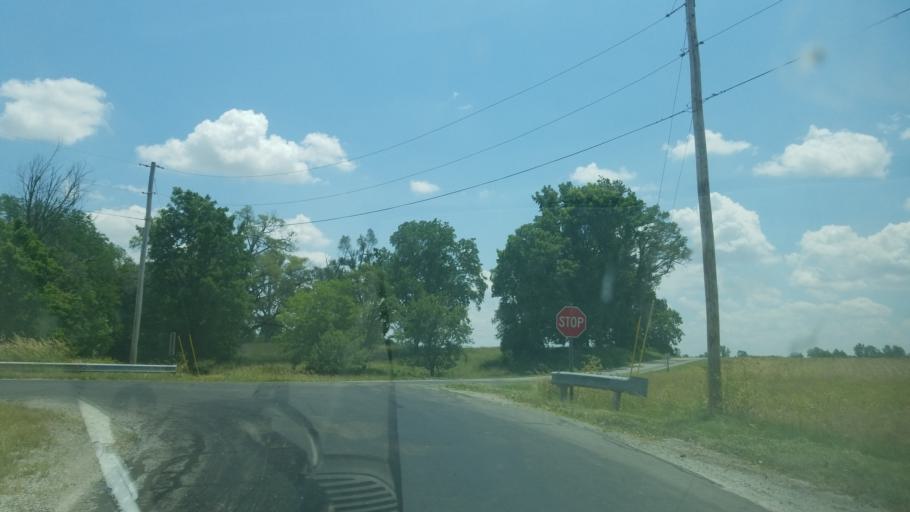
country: US
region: Ohio
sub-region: Hardin County
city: Kenton
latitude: 40.6331
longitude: -83.5619
